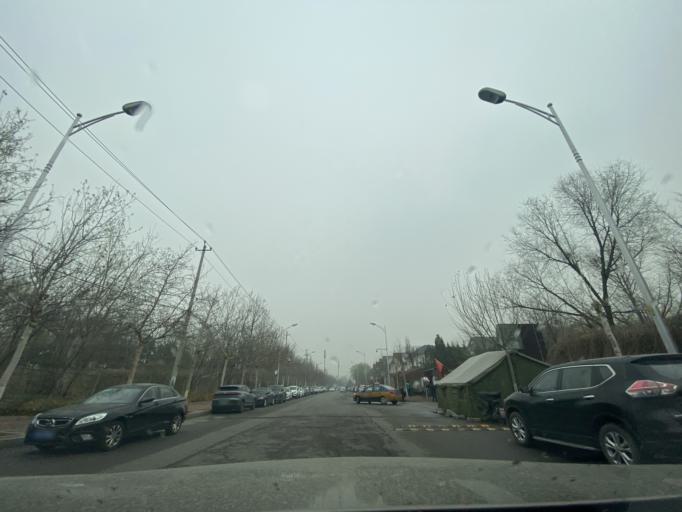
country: CN
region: Beijing
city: Sijiqing
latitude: 39.9583
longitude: 116.2333
